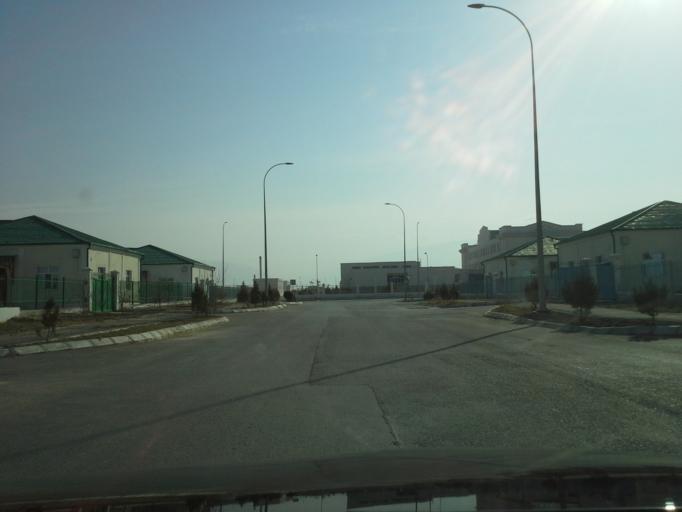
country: TM
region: Ahal
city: Abadan
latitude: 38.1724
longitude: 58.0485
